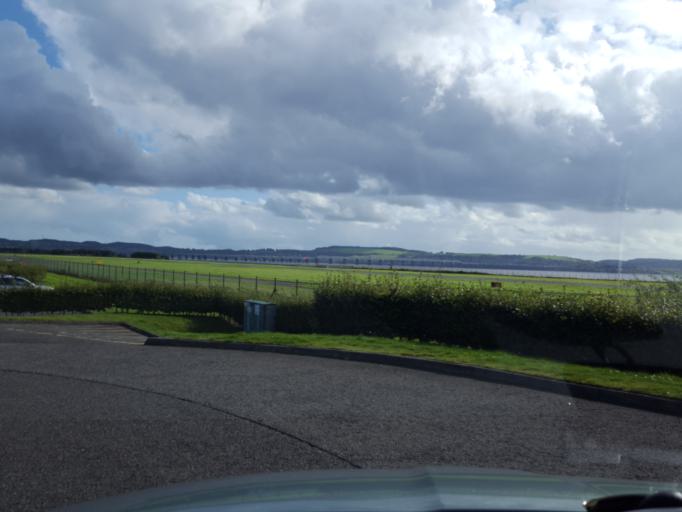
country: GB
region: Scotland
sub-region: Dundee City
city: Dundee
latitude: 56.4537
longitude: -3.0234
